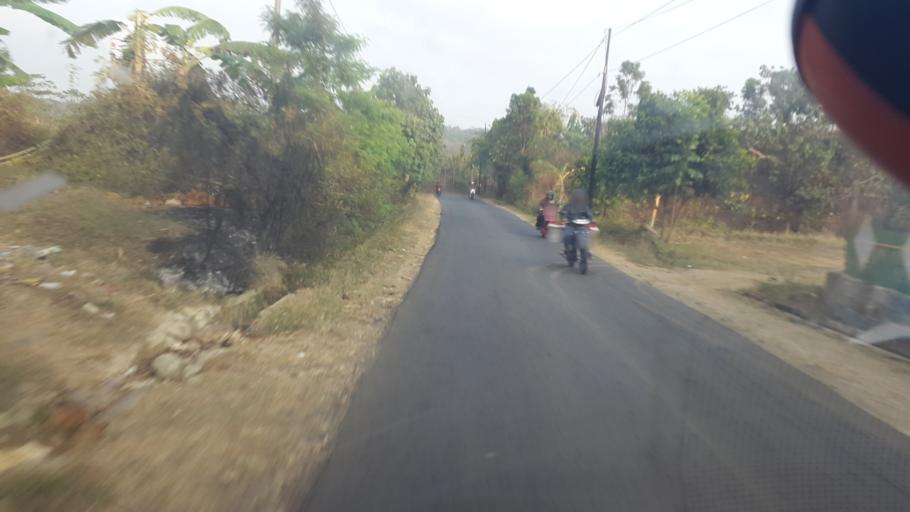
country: ID
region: West Java
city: Pondokaso
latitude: -7.3535
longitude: 106.5367
